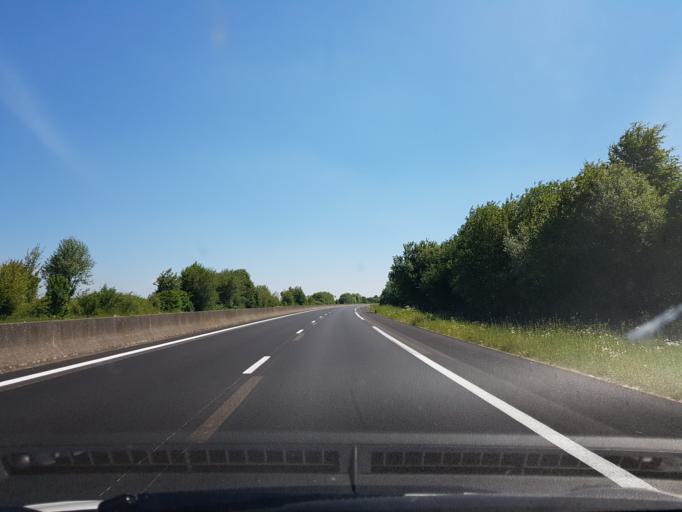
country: FR
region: Picardie
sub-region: Departement de l'Aisne
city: Vermand
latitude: 49.8466
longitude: 3.0945
